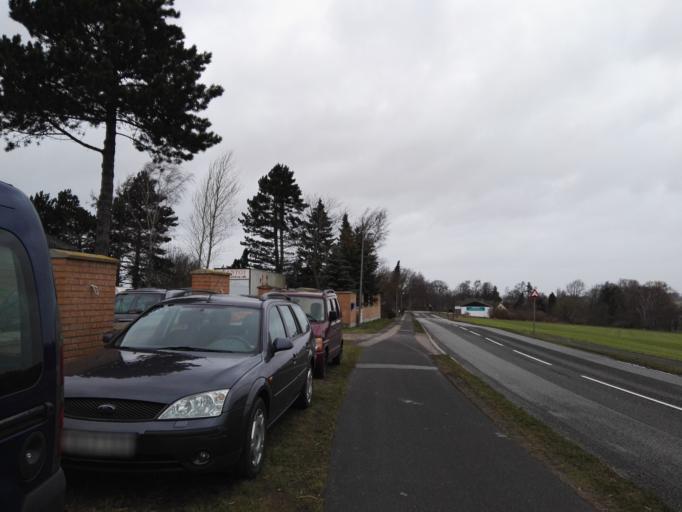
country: DK
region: Zealand
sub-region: Lejre Kommune
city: Ejby
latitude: 55.6894
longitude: 11.9121
